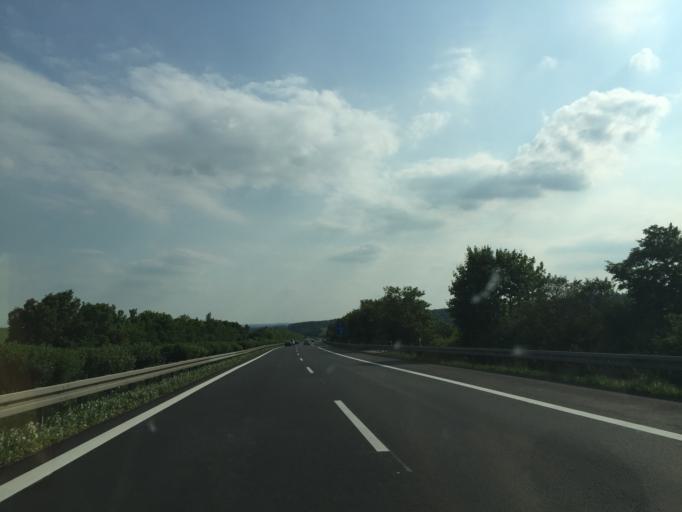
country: DE
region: Baden-Wuerttemberg
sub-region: Regierungsbezirk Stuttgart
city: Grossrinderfeld
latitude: 49.6844
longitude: 9.7836
